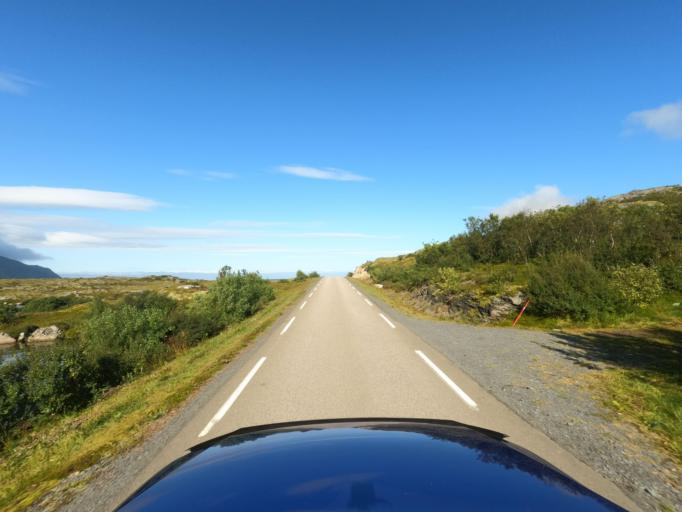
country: NO
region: Nordland
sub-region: Vestvagoy
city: Evjen
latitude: 68.3109
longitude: 14.0957
